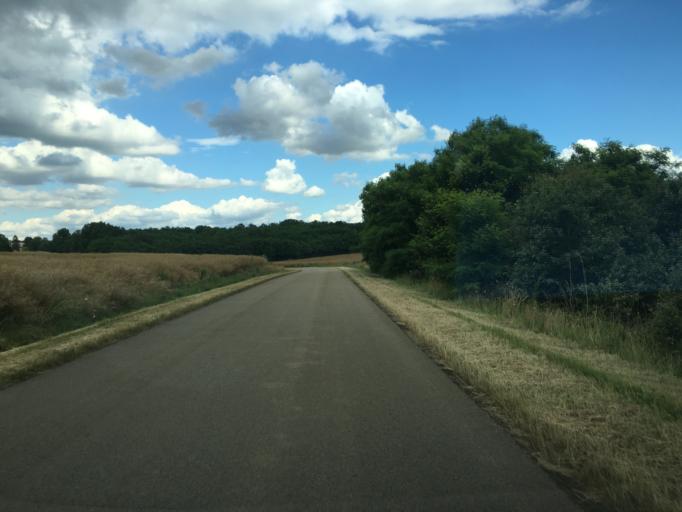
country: FR
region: Bourgogne
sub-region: Departement de l'Yonne
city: Charbuy
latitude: 47.8233
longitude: 3.4311
